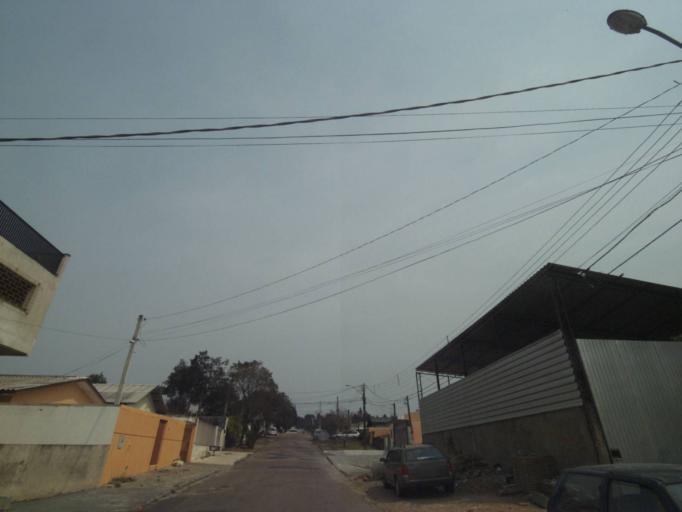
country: BR
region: Parana
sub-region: Sao Jose Dos Pinhais
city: Sao Jose dos Pinhais
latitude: -25.5204
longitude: -49.2855
